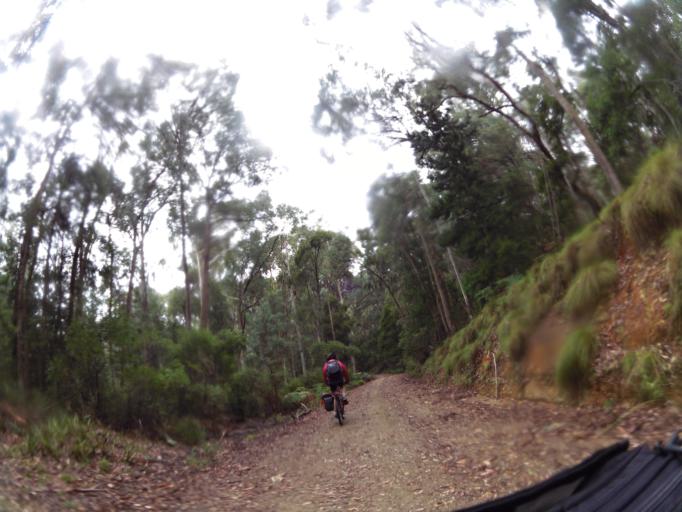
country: AU
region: New South Wales
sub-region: Greater Hume Shire
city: Holbrook
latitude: -36.1975
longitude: 147.5220
